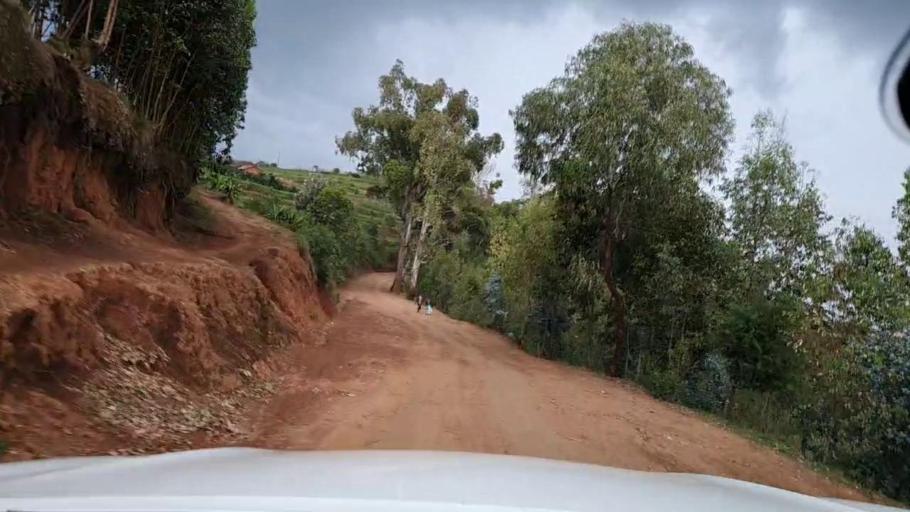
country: BI
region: Kayanza
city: Kayanza
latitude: -2.7903
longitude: 29.5258
